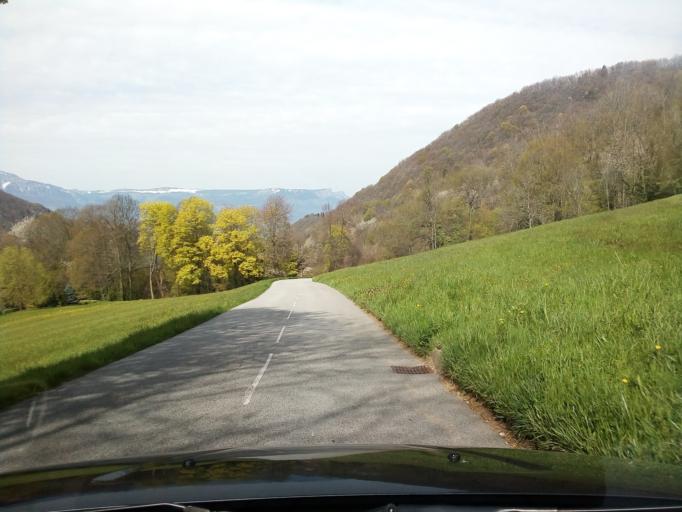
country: FR
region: Rhone-Alpes
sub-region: Departement de l'Isere
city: Herbeys
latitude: 45.1622
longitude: 5.8282
